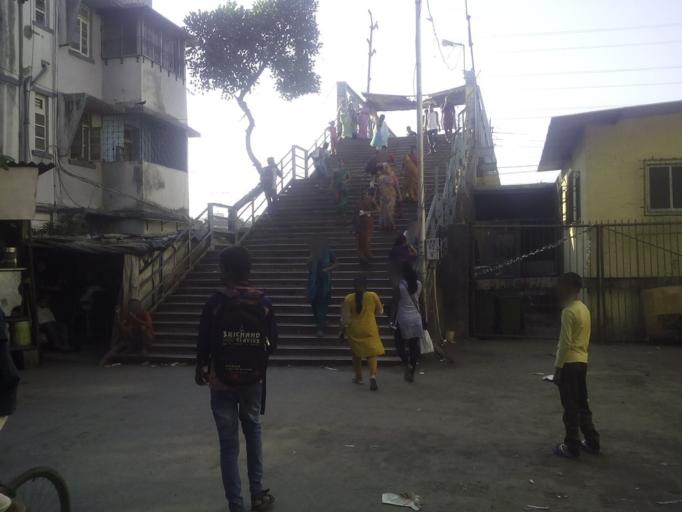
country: IN
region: Maharashtra
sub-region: Mumbai Suburban
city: Mumbai
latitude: 19.0402
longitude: 72.8596
